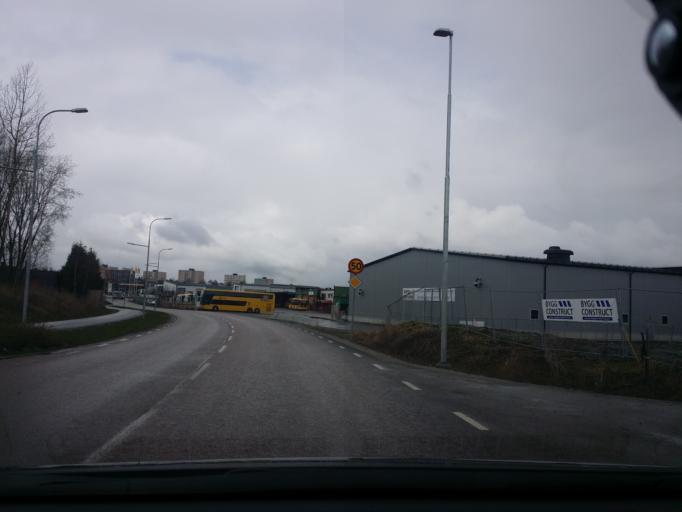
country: SE
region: Uppsala
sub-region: Enkopings Kommun
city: Enkoping
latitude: 59.6467
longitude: 17.0912
